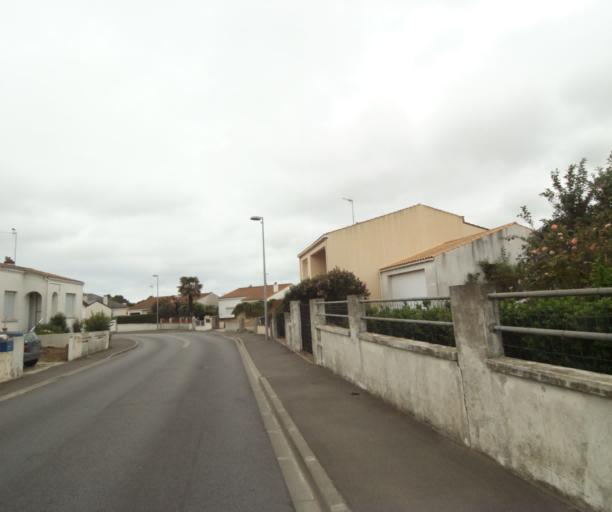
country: FR
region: Pays de la Loire
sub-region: Departement de la Vendee
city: Les Sables-d'Olonne
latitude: 46.5008
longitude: -1.7712
